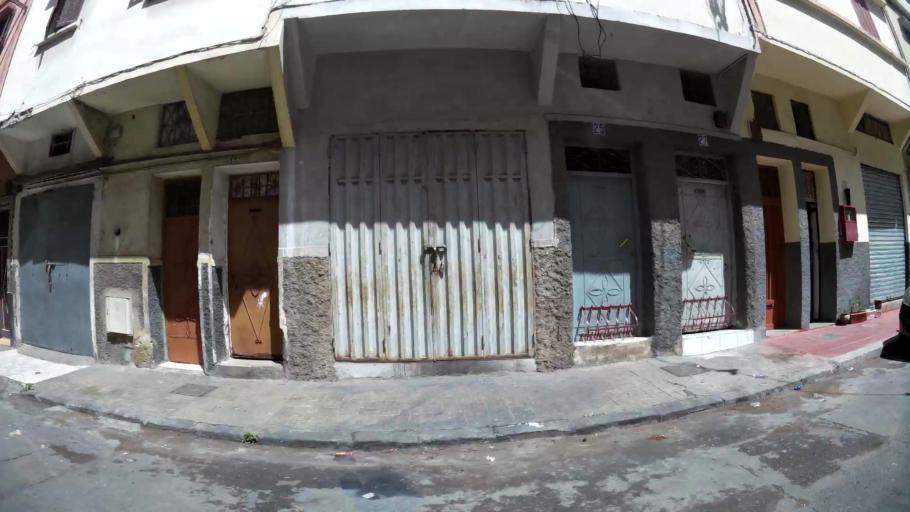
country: MA
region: Grand Casablanca
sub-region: Casablanca
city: Casablanca
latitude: 33.5599
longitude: -7.6029
